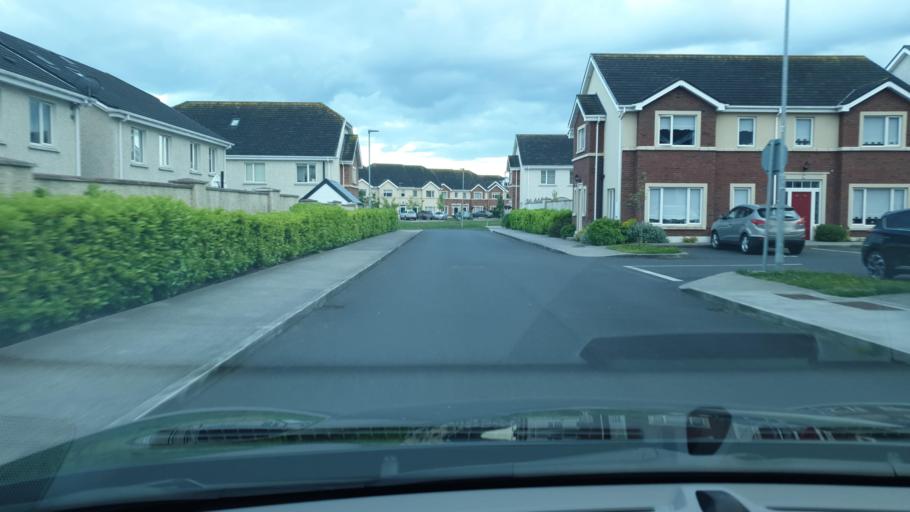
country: IE
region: Leinster
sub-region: An Mhi
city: Ashbourne
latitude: 53.5038
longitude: -6.3843
